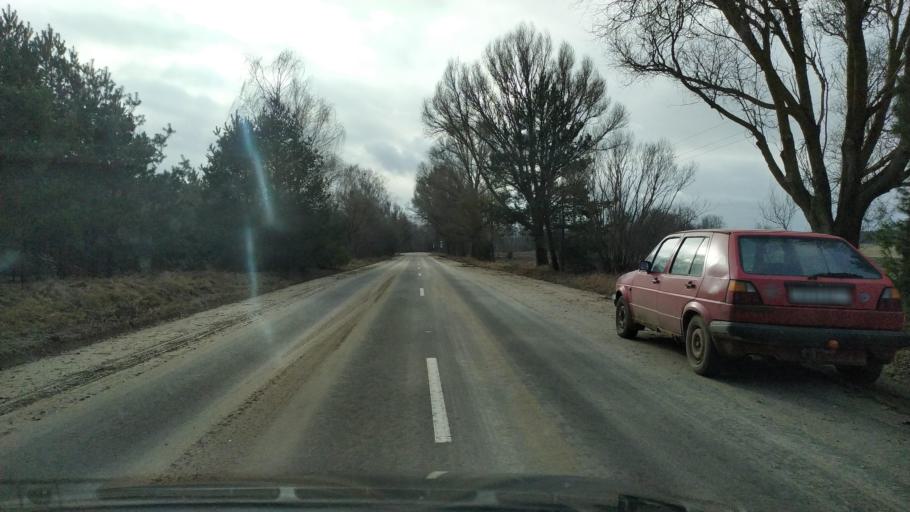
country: BY
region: Brest
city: Kamyanyets
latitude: 52.4026
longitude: 23.9037
